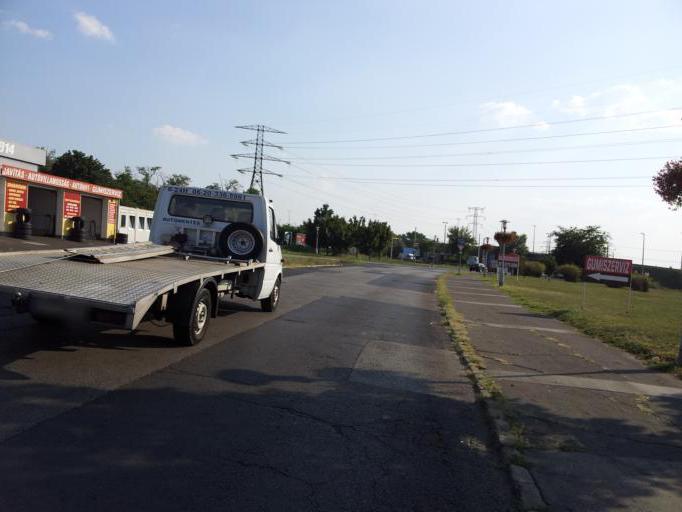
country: HU
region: Budapest
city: Budapest XX. keruelet
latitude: 47.4580
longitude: 19.1142
